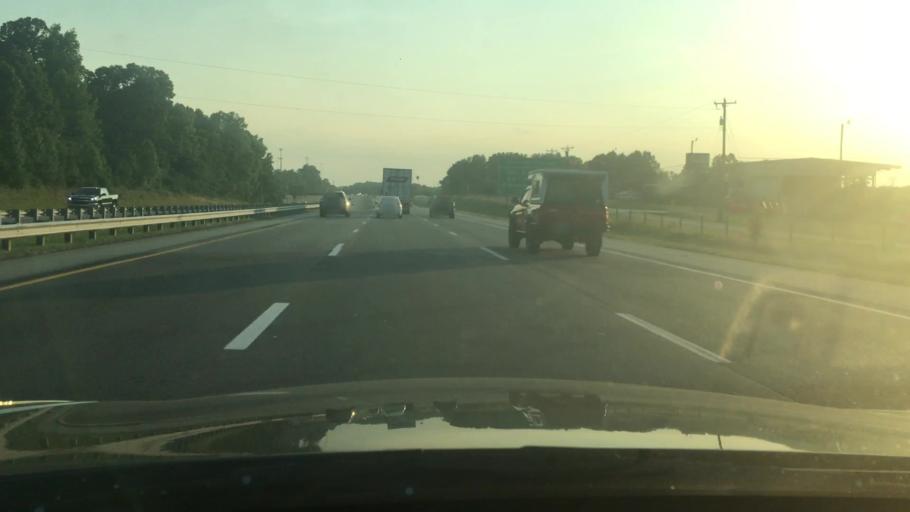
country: US
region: North Carolina
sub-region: Guilford County
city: Forest Oaks
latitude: 36.0540
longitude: -79.7253
